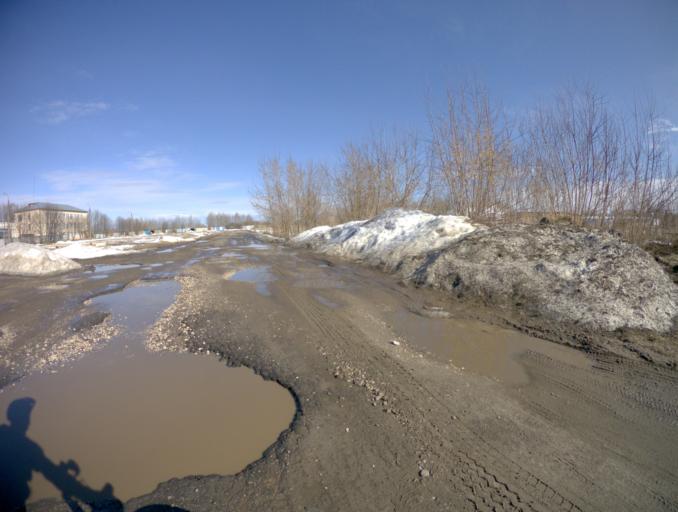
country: RU
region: Vladimir
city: Suzdal'
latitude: 56.4449
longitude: 40.4583
